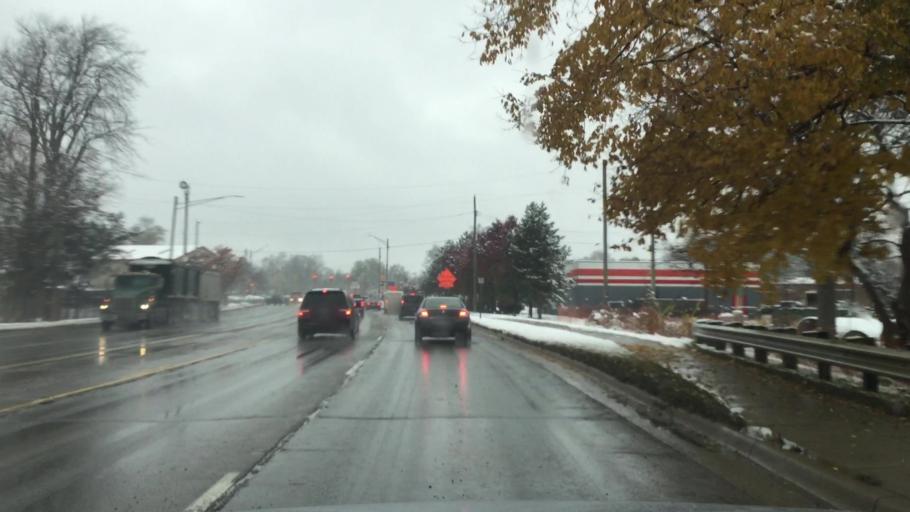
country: US
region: Michigan
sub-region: Oakland County
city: Lake Orion
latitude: 42.7832
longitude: -83.2407
